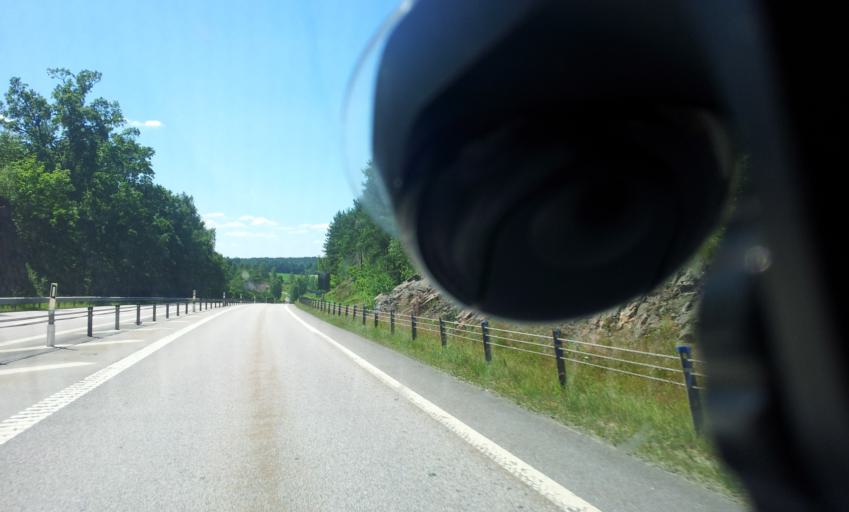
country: SE
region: Kalmar
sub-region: Vasterviks Kommun
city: Forserum
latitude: 58.0129
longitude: 16.5095
